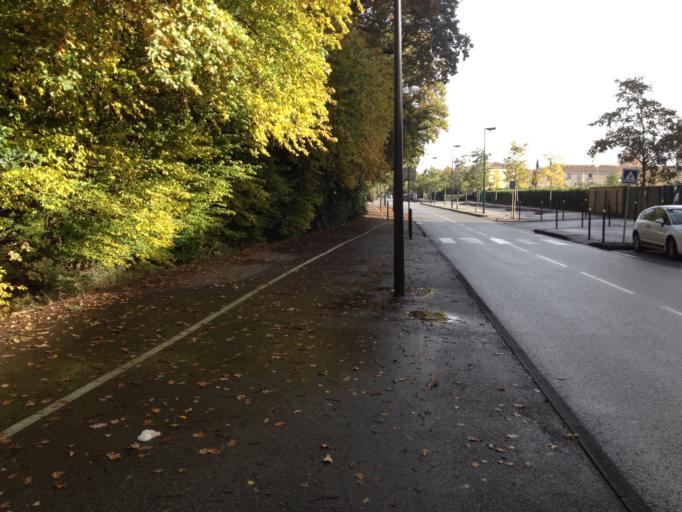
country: FR
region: Provence-Alpes-Cote d'Azur
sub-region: Departement du Vaucluse
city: Orange
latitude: 44.1336
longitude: 4.8188
